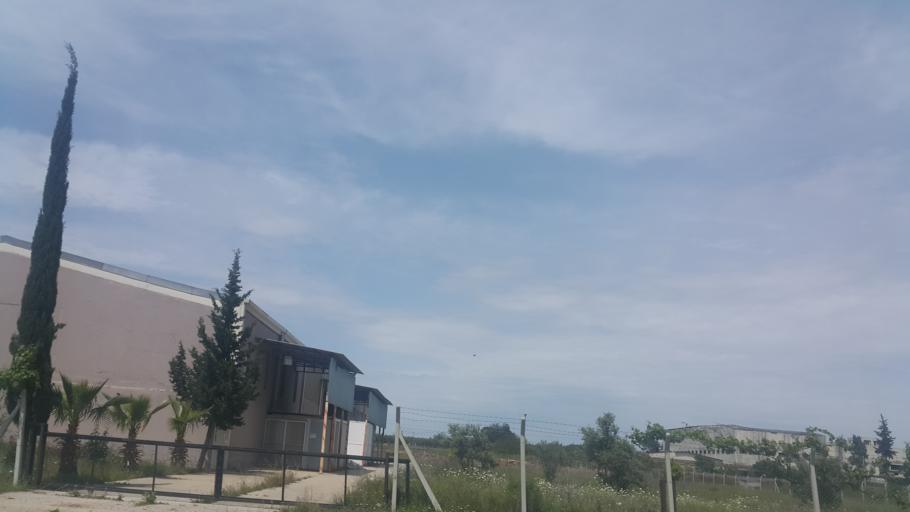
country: TR
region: Adana
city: Yakapinar
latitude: 36.9716
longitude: 35.5195
